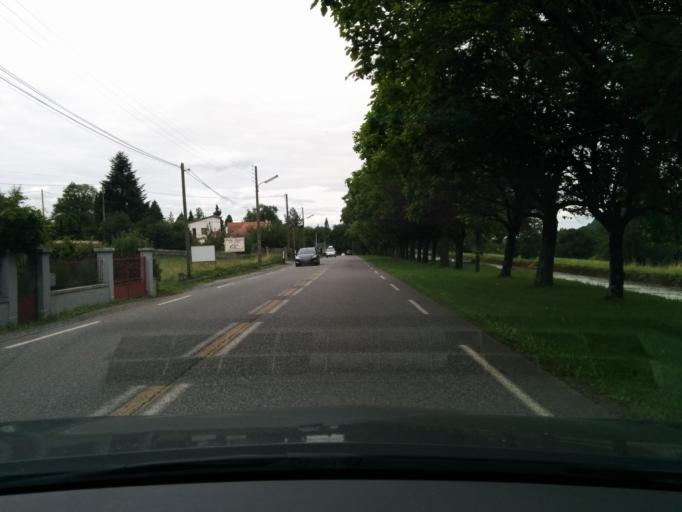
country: FR
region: Midi-Pyrenees
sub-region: Departement des Hautes-Pyrenees
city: La Barthe-de-Neste
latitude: 43.0220
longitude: 0.3720
